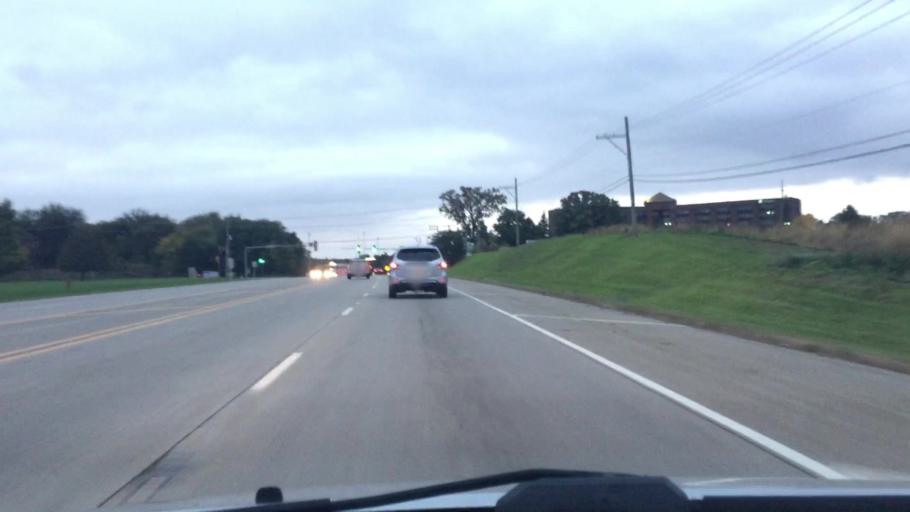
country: US
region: Illinois
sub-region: McHenry County
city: Crystal Lake
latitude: 42.2173
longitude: -88.2865
